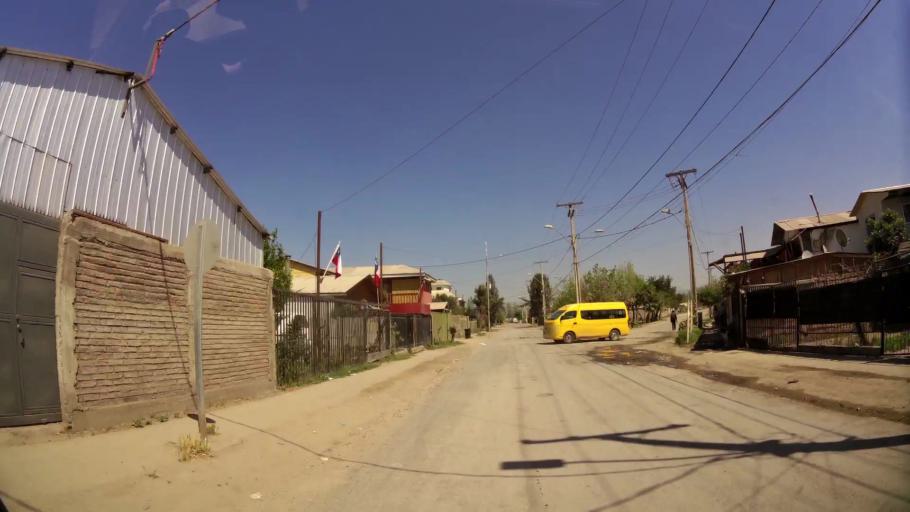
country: CL
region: Santiago Metropolitan
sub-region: Provincia de Talagante
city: Penaflor
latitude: -33.5913
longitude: -70.8121
